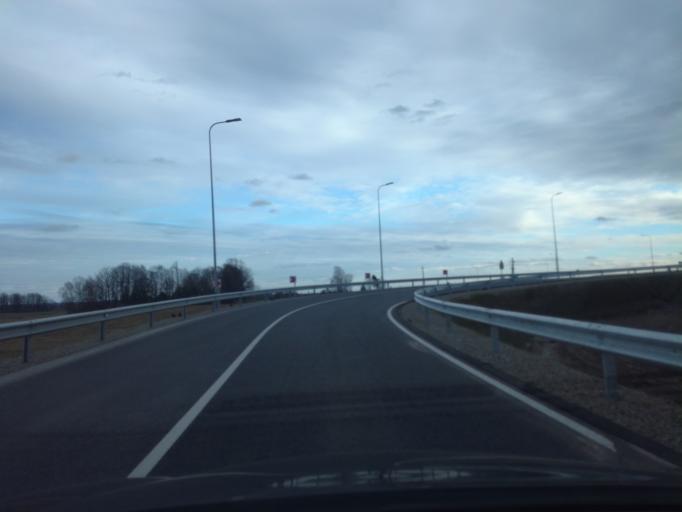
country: LT
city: Ezerelis
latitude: 54.7255
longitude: 23.6868
